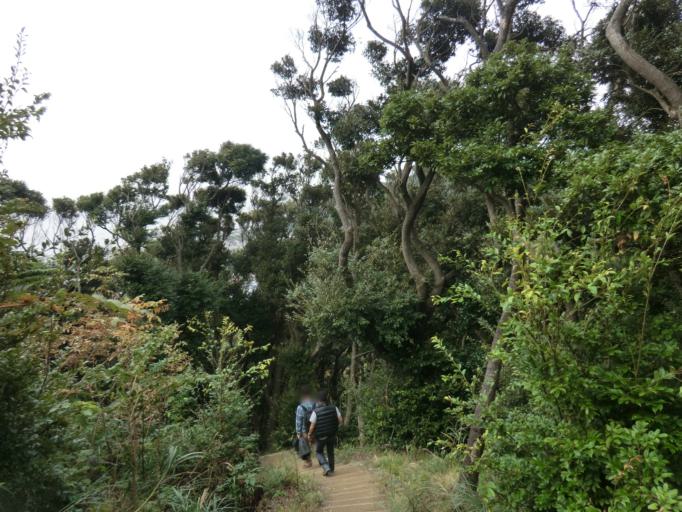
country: JP
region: Chiba
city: Futtsu
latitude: 35.1649
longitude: 139.8287
